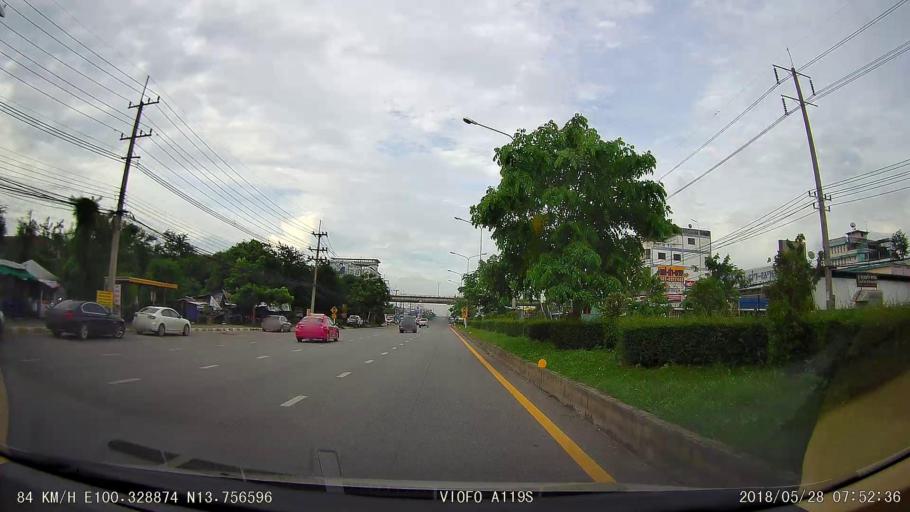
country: TH
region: Bangkok
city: Thawi Watthana
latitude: 13.7564
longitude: 100.3289
